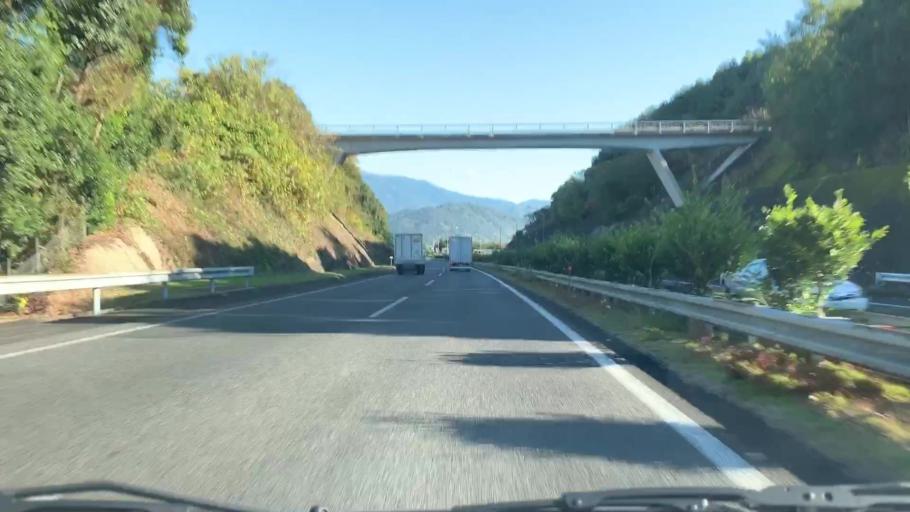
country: JP
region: Saga Prefecture
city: Takeocho-takeo
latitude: 33.2500
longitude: 130.0757
